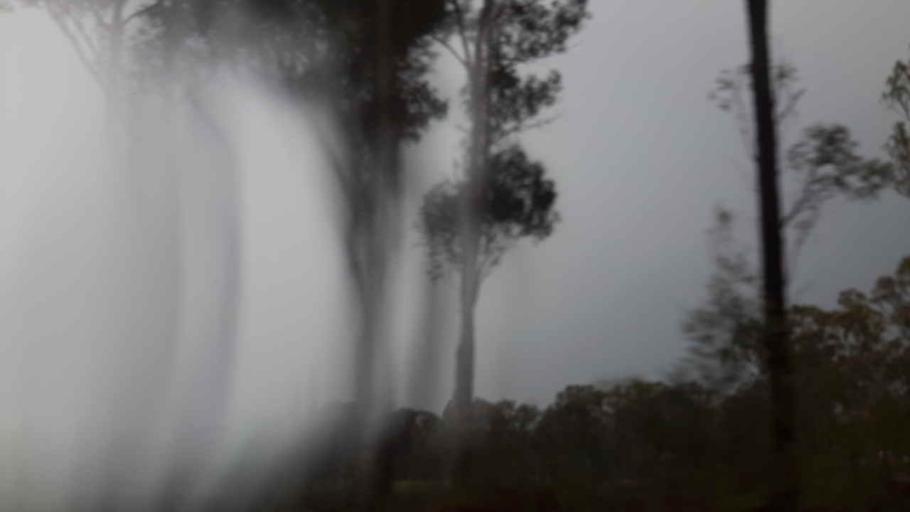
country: AU
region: New South Wales
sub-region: Wollondilly
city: Douglas Park
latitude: -34.2000
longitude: 150.7087
